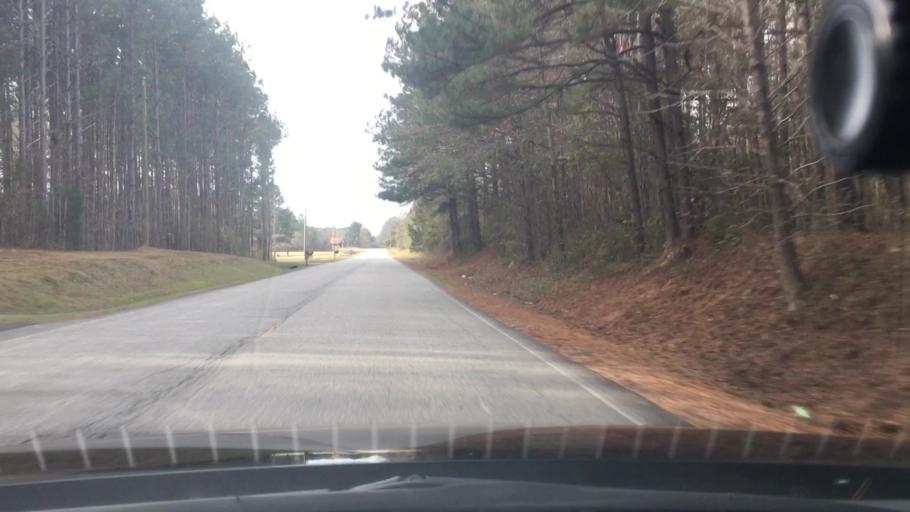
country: US
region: Georgia
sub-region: Coweta County
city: Senoia
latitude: 33.2856
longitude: -84.4339
